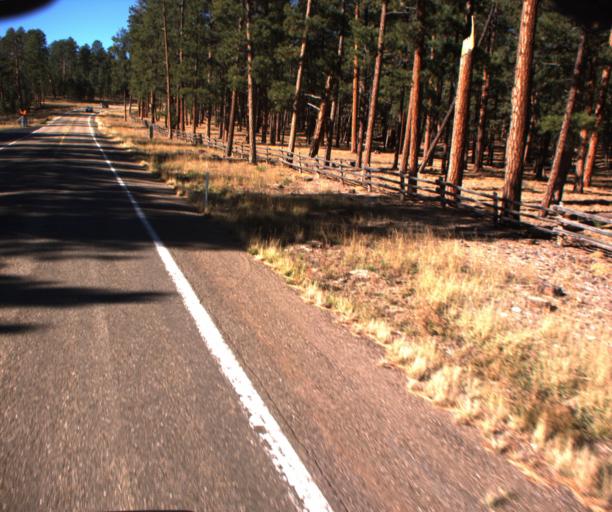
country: US
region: Arizona
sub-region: Coconino County
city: Fredonia
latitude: 36.7143
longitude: -112.2100
